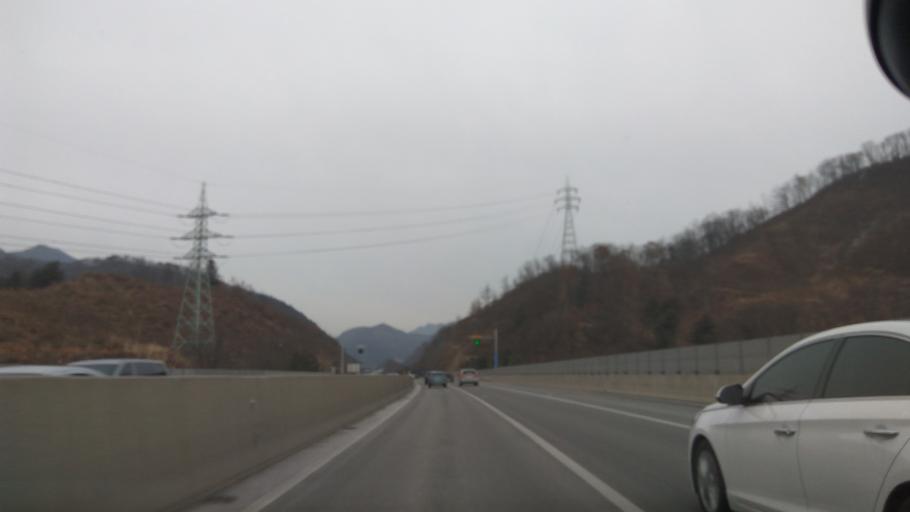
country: KR
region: Gyeonggi-do
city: Hwado
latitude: 37.6356
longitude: 127.3995
